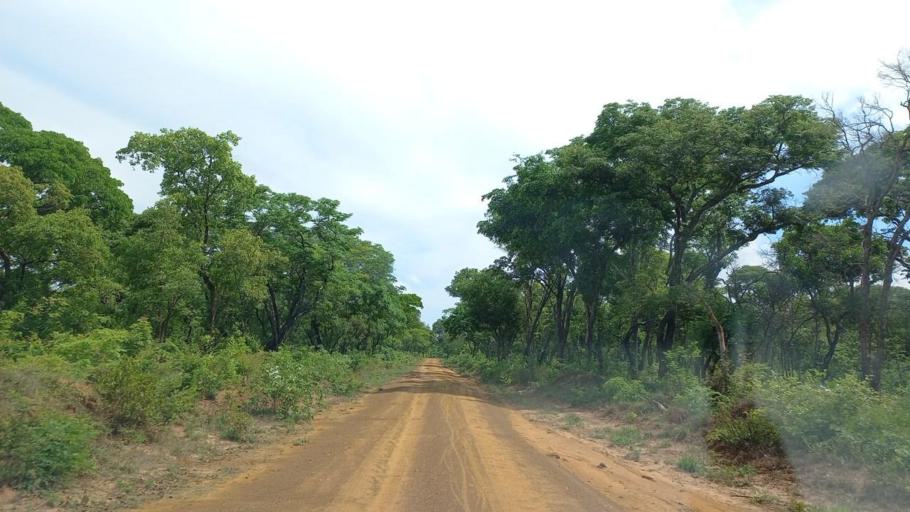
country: ZM
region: North-Western
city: Kabompo
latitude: -13.5409
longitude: 24.0997
